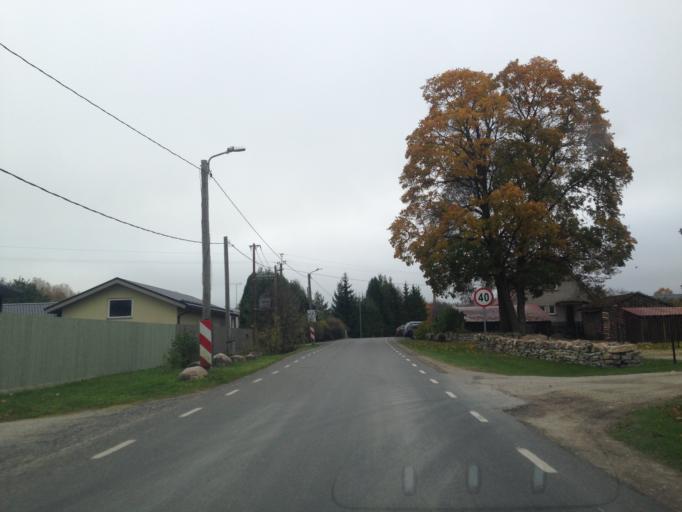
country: EE
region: Harju
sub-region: Harku vald
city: Tabasalu
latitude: 59.3786
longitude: 24.5390
